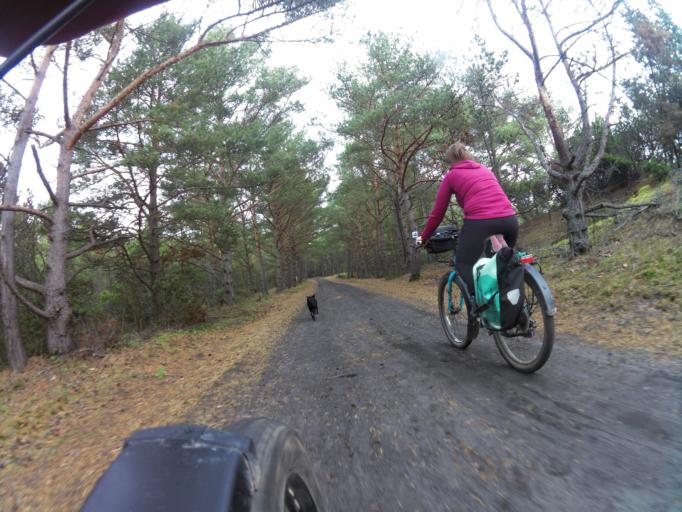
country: PL
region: Pomeranian Voivodeship
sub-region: Powiat pucki
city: Hel
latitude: 54.6200
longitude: 18.8197
